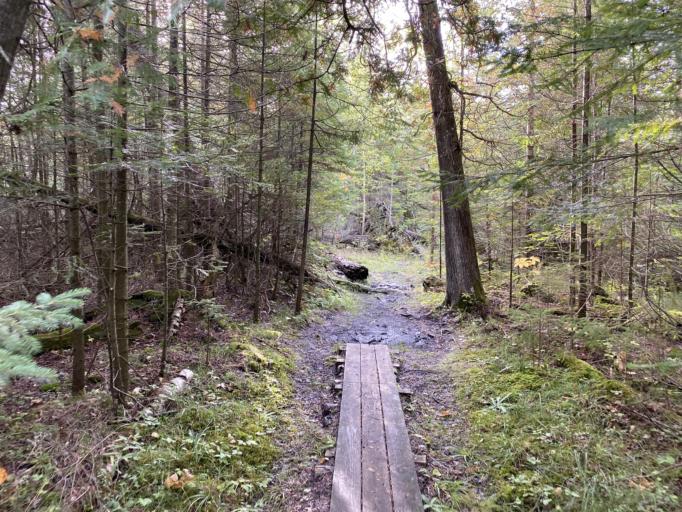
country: US
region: Michigan
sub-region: Mackinac County
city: Saint Ignace
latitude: 45.7420
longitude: -84.8906
